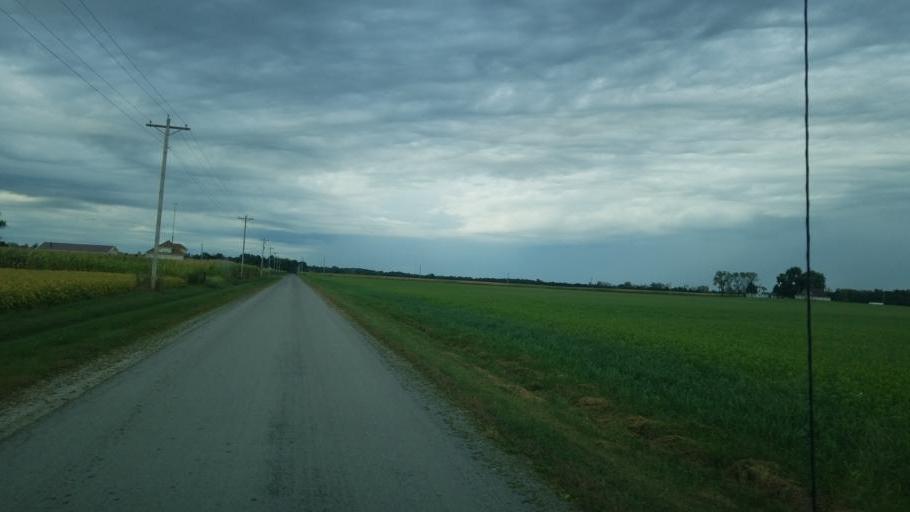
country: US
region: Ohio
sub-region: Wyandot County
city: Carey
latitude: 40.8968
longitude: -83.3571
